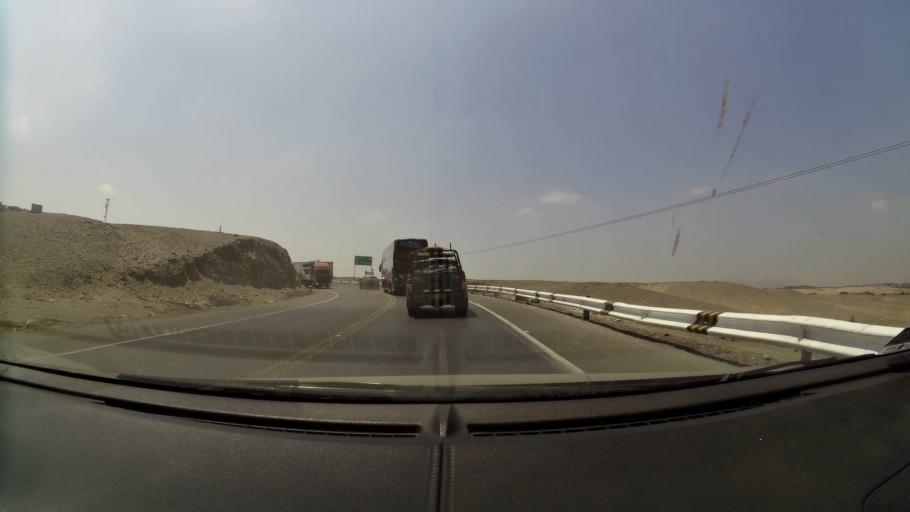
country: PE
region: La Libertad
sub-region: Provincia de Pacasmayo
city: Pacasmayo
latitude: -7.3922
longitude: -79.5554
